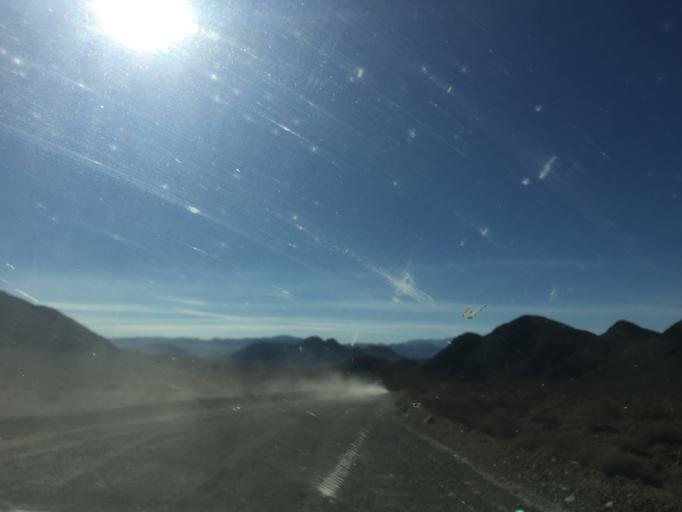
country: US
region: California
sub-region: Inyo County
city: Lone Pine
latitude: 36.7784
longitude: -117.5285
